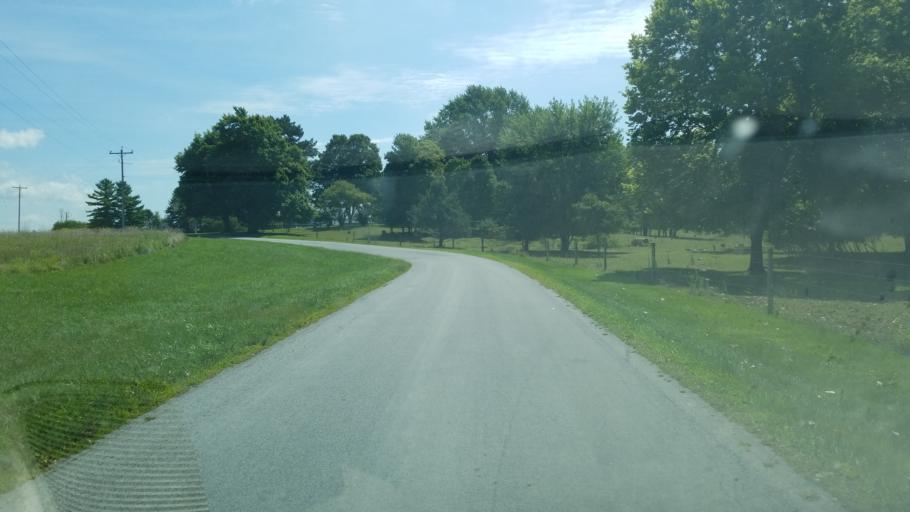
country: US
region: Ohio
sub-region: Hardin County
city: Kenton
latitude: 40.6128
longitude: -83.6350
